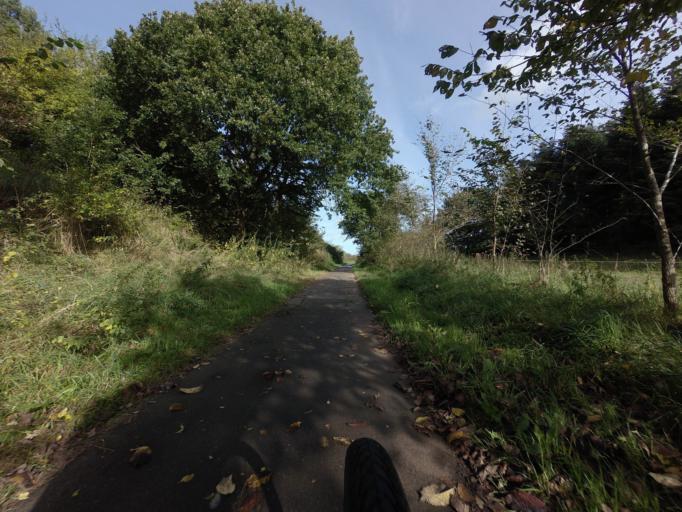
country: DK
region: Central Jutland
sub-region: Viborg Kommune
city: Bjerringbro
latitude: 56.4677
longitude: 9.5898
